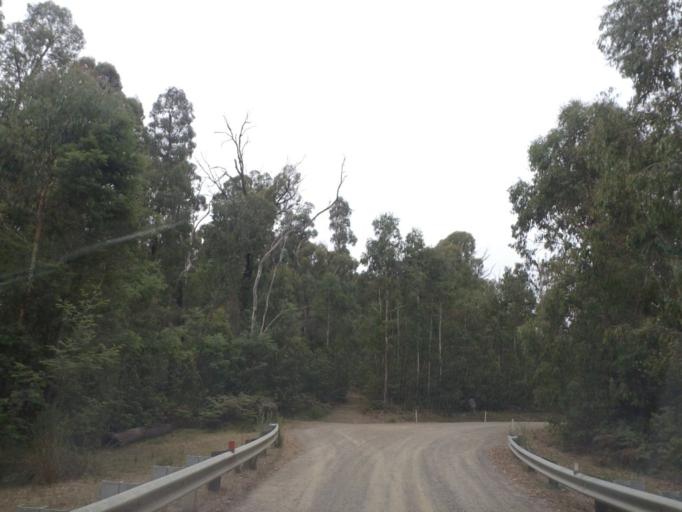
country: AU
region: Victoria
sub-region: Yarra Ranges
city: Healesville
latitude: -37.4242
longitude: 145.5692
